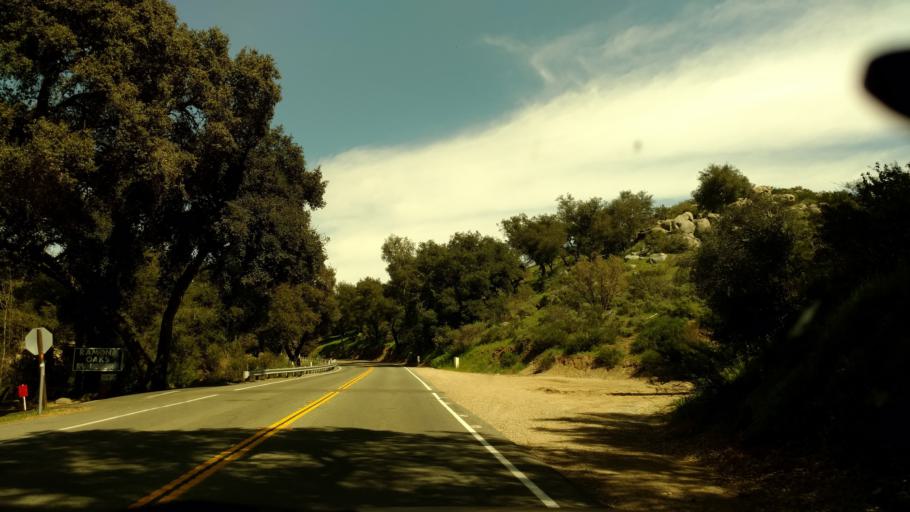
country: US
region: California
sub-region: San Diego County
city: San Diego Country Estates
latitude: 33.0731
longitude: -116.8041
